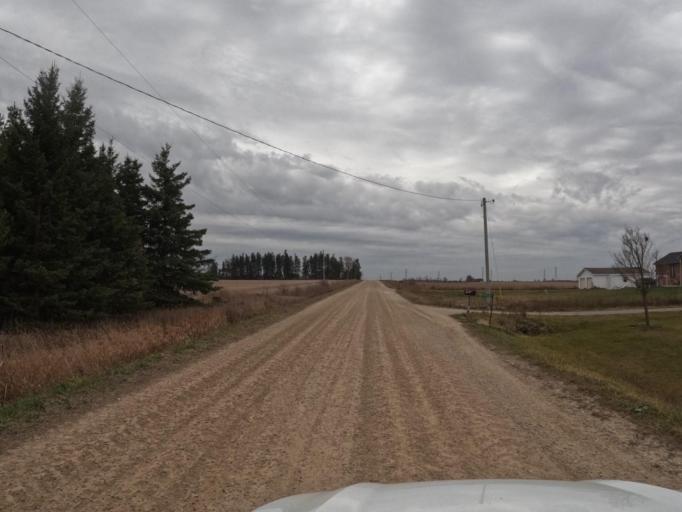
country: CA
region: Ontario
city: Shelburne
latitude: 44.0050
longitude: -80.3881
